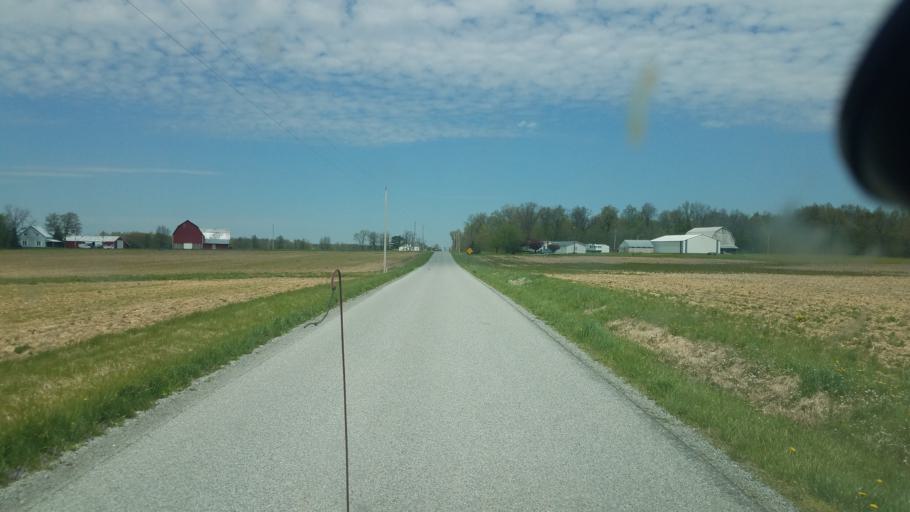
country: US
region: Ohio
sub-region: Hardin County
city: Ada
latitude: 40.7941
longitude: -83.8990
